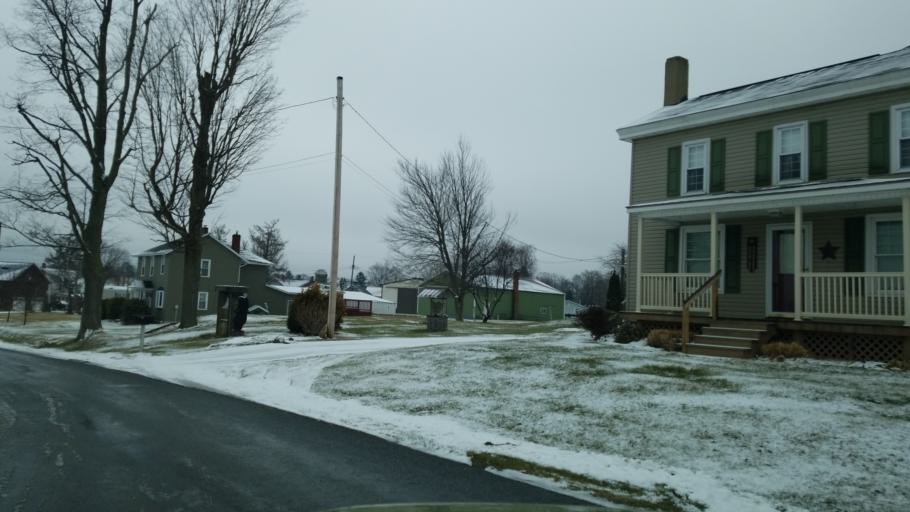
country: US
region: Pennsylvania
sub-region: Jefferson County
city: Sykesville
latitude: 41.0239
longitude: -78.7865
